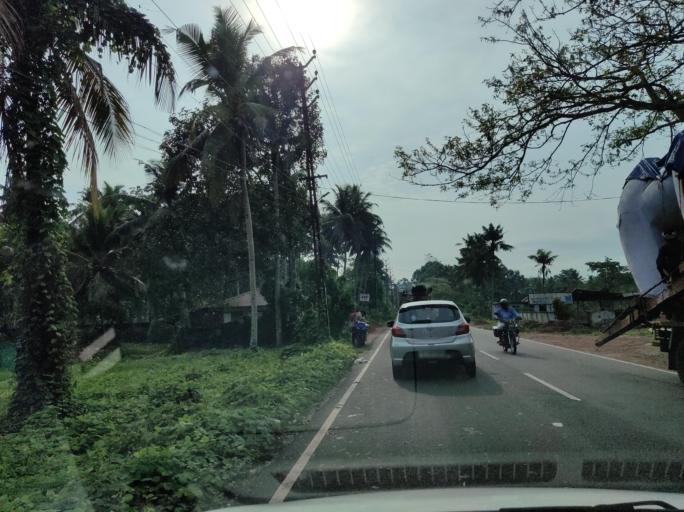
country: IN
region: Kerala
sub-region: Alappuzha
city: Kattanam
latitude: 9.1734
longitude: 76.5862
